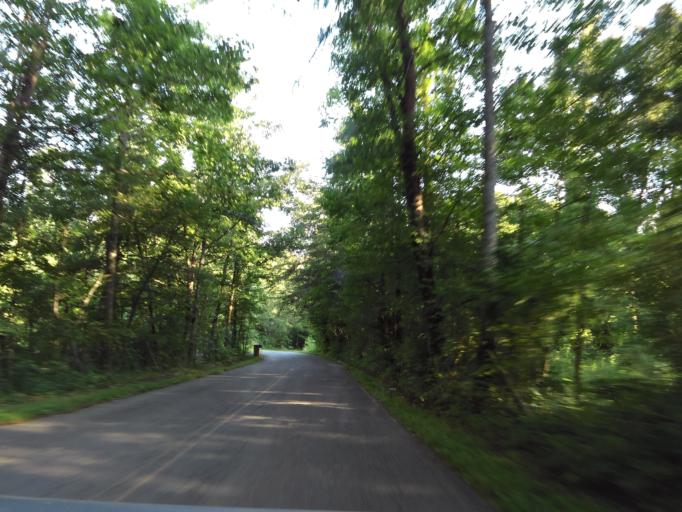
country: US
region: Tennessee
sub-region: Blount County
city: Maryville
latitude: 35.6200
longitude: -83.9398
